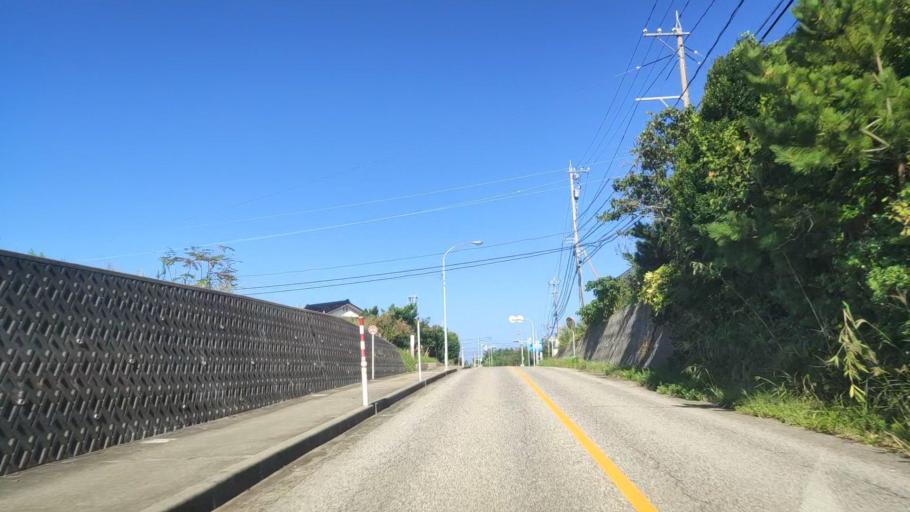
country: JP
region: Ishikawa
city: Hakui
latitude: 37.0520
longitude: 136.7329
